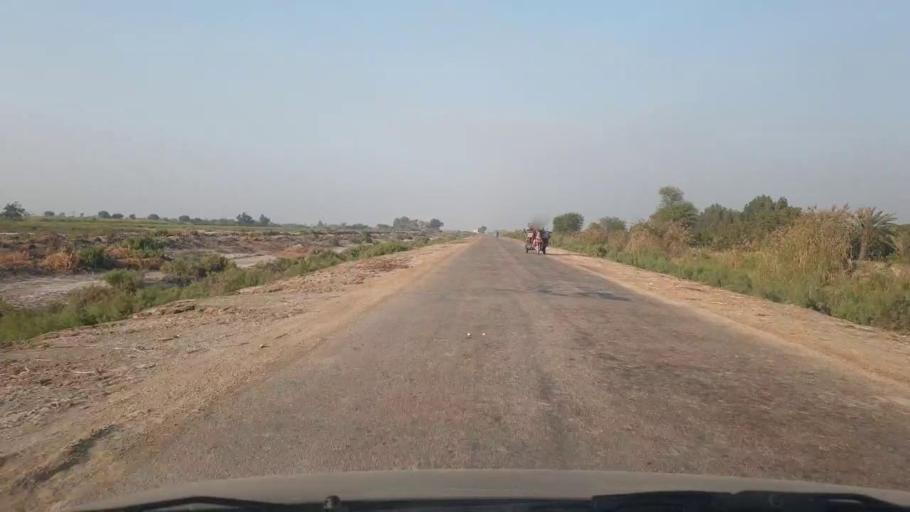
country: PK
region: Sindh
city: Mirwah Gorchani
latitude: 25.3414
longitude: 69.1697
